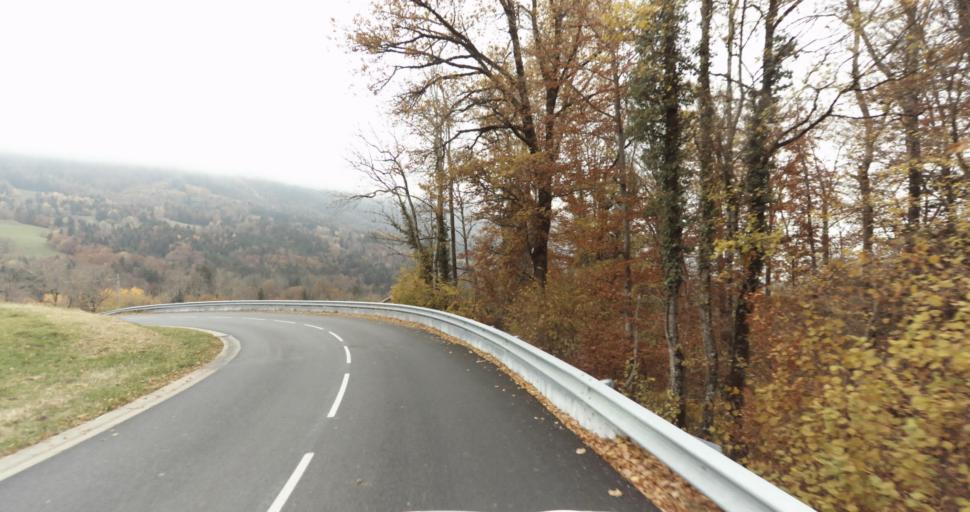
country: FR
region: Rhone-Alpes
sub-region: Departement de la Haute-Savoie
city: Saint-Jorioz
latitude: 45.7936
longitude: 6.1479
